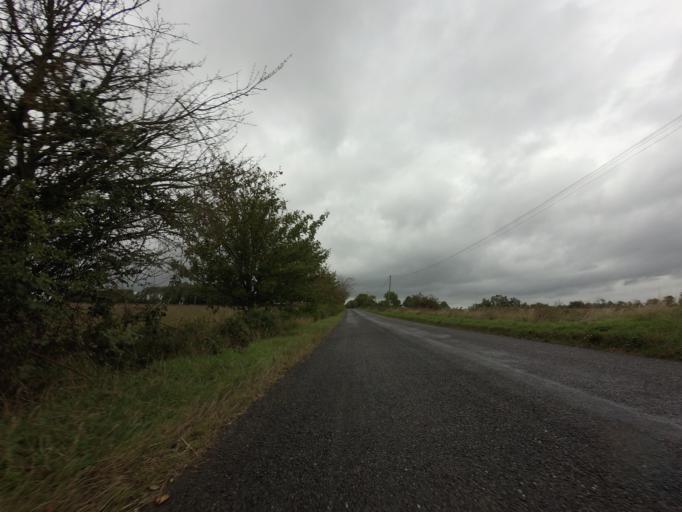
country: GB
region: England
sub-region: Cambridgeshire
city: Wimpole
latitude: 52.1749
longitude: -0.0271
